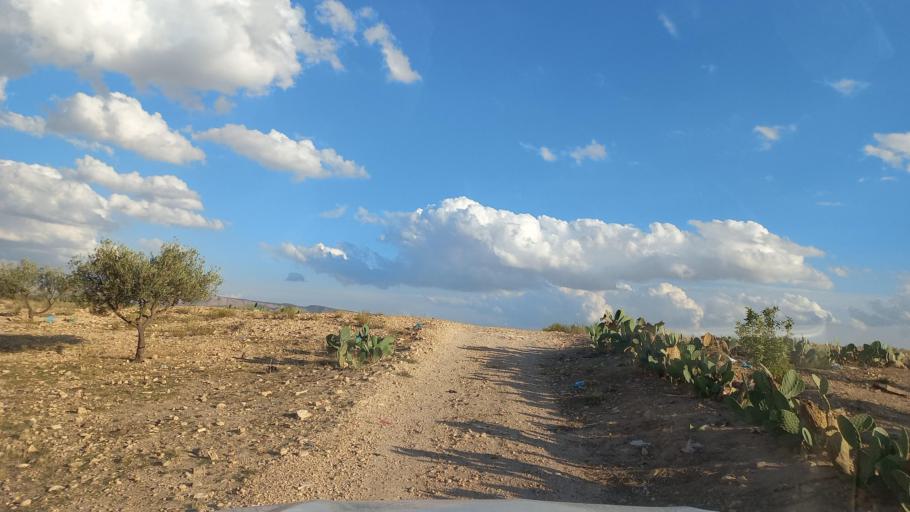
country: TN
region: Al Qasrayn
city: Sbiba
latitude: 35.3914
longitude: 9.0565
